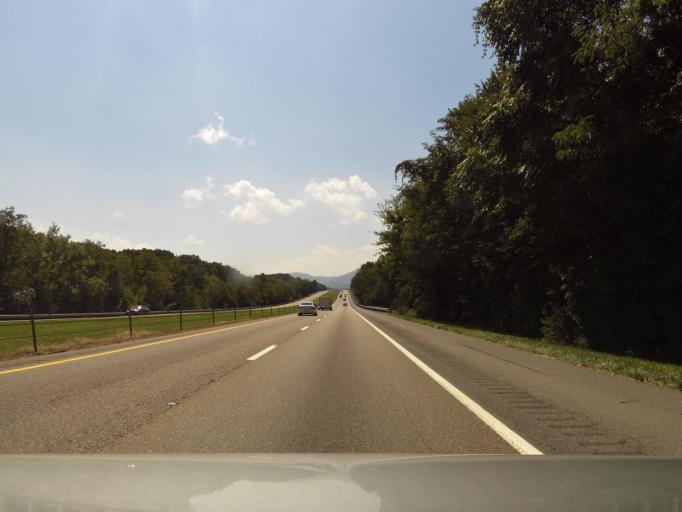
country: US
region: Tennessee
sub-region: Jefferson County
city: White Pine
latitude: 36.0143
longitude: -83.2951
